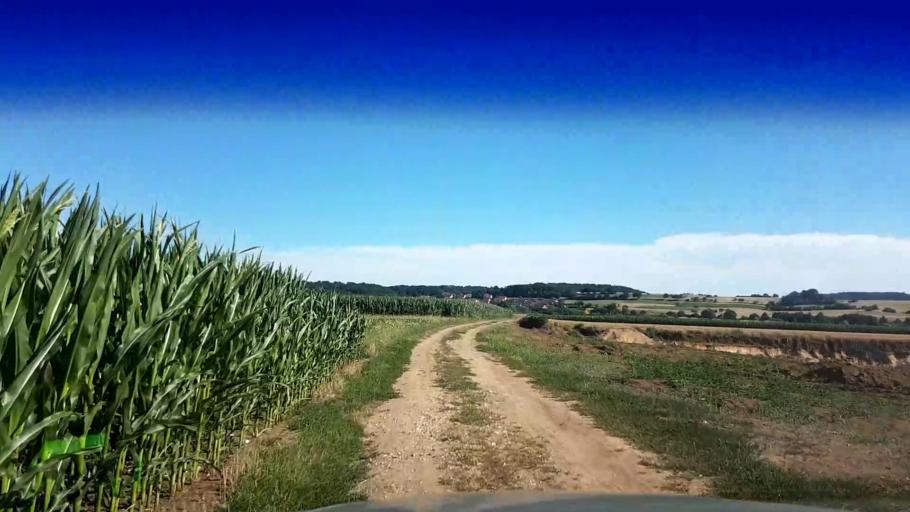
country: DE
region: Bavaria
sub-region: Upper Franconia
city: Viereth-Trunstadt
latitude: 49.9348
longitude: 10.7621
